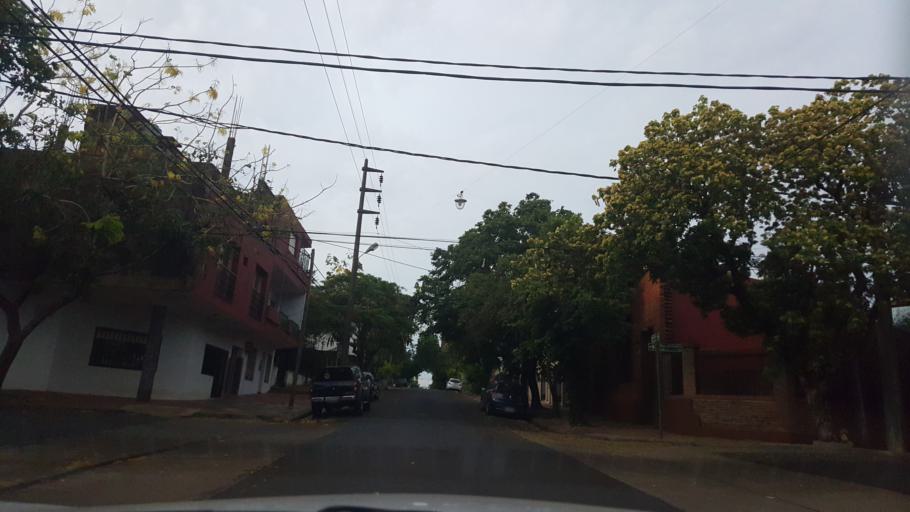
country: AR
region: Misiones
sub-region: Departamento de Capital
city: Posadas
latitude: -27.3743
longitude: -55.8893
